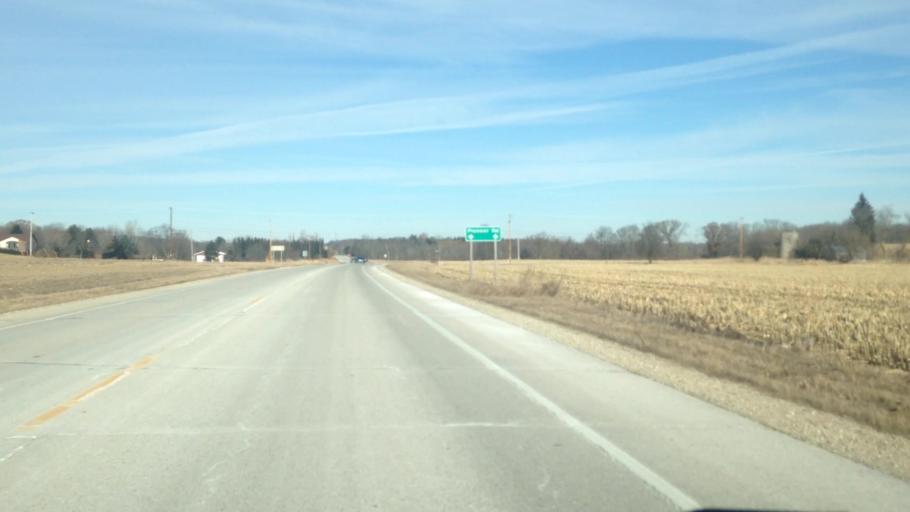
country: US
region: Wisconsin
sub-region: Washington County
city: Slinger
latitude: 43.2791
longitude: -88.2613
